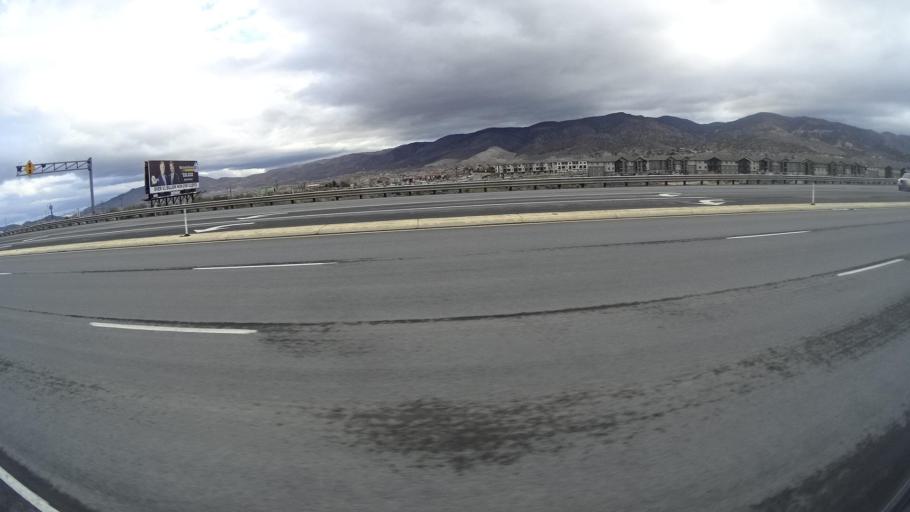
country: US
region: Nevada
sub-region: Storey County
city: Virginia City
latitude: 39.4015
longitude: -119.7458
